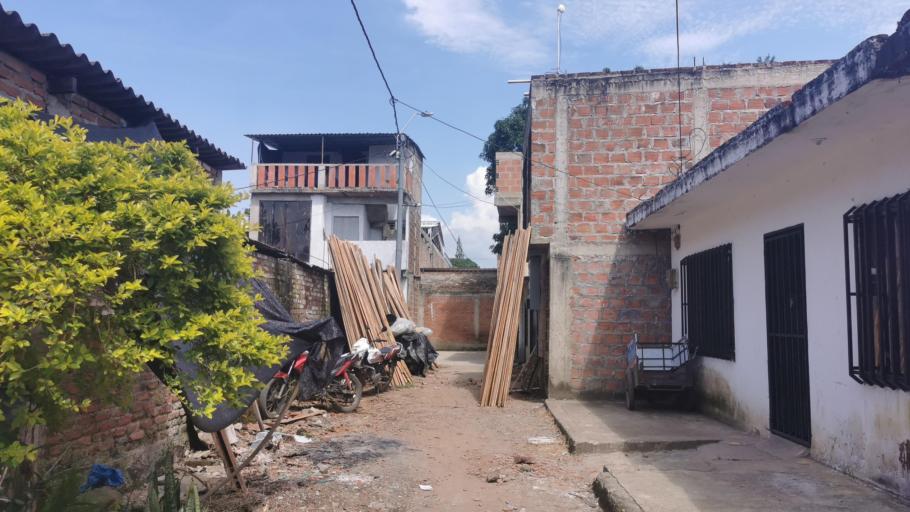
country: CO
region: Valle del Cauca
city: Jamundi
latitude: 3.2626
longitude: -76.5314
